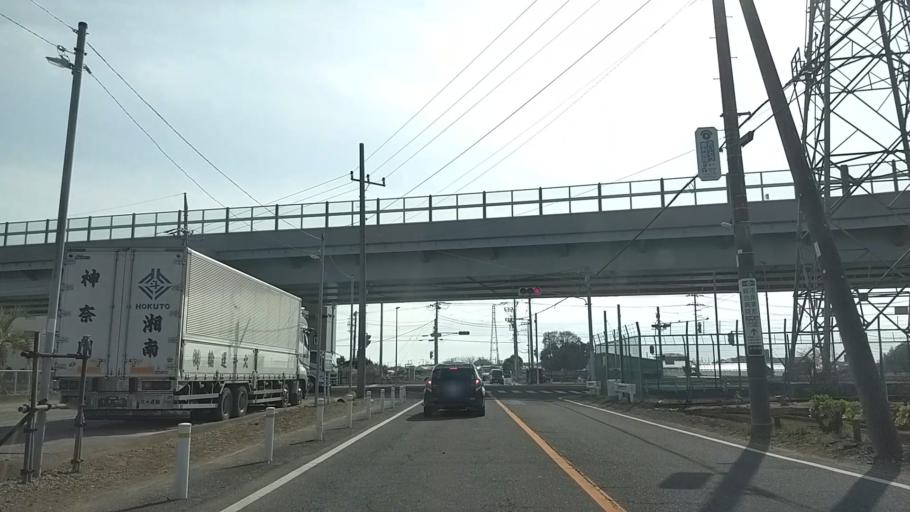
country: JP
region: Kanagawa
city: Chigasaki
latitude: 35.3521
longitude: 139.3848
